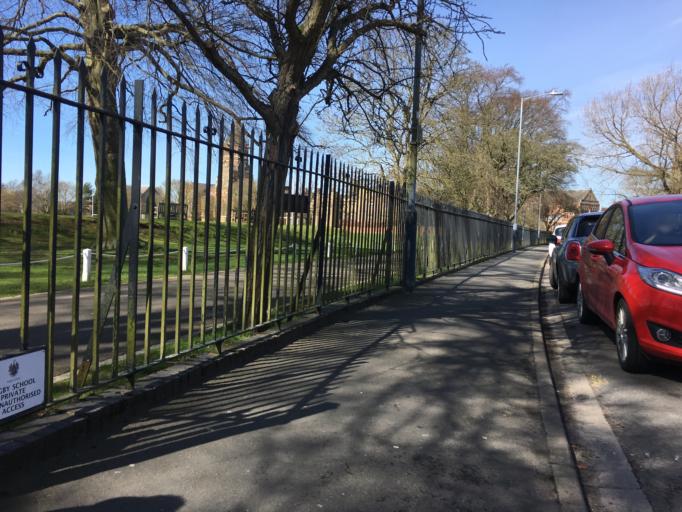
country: GB
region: England
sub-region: Warwickshire
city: Rugby
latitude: 52.3689
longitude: -1.2614
